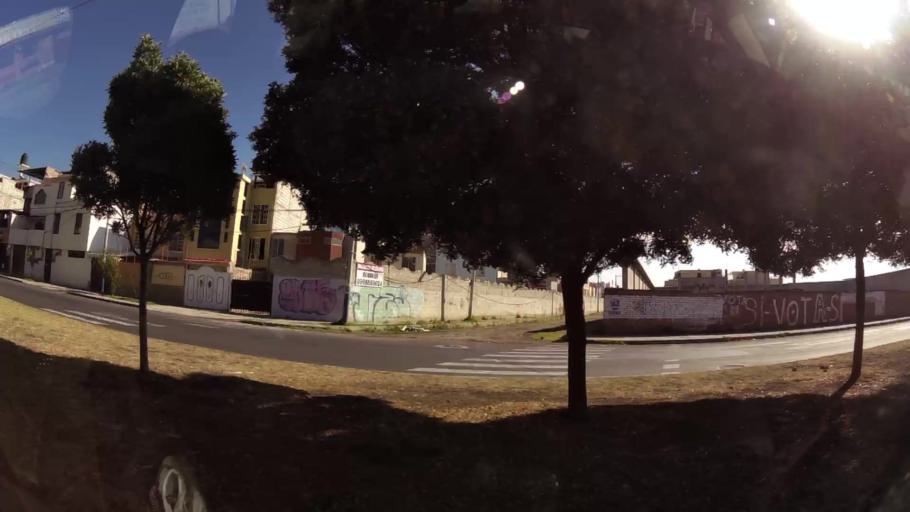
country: EC
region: Chimborazo
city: Riobamba
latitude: -1.6485
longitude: -78.6796
